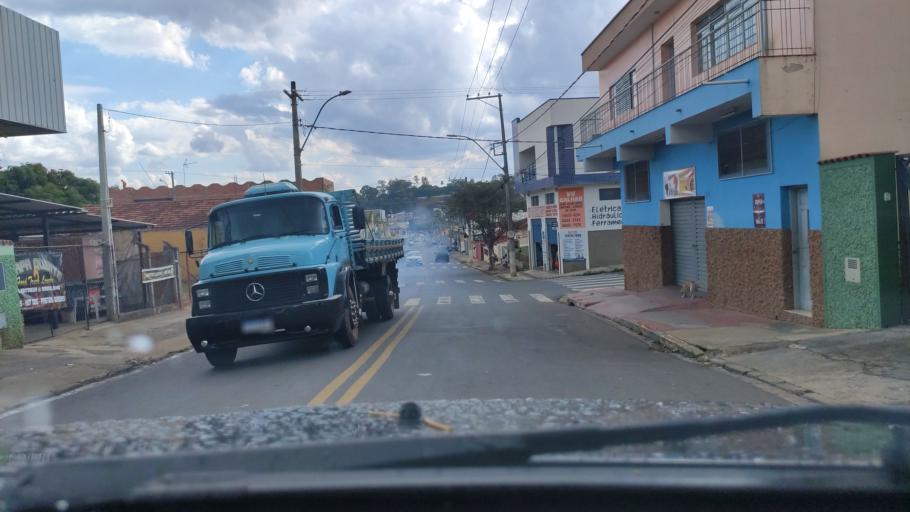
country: BR
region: Sao Paulo
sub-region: Itapira
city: Itapira
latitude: -22.4381
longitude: -46.8120
